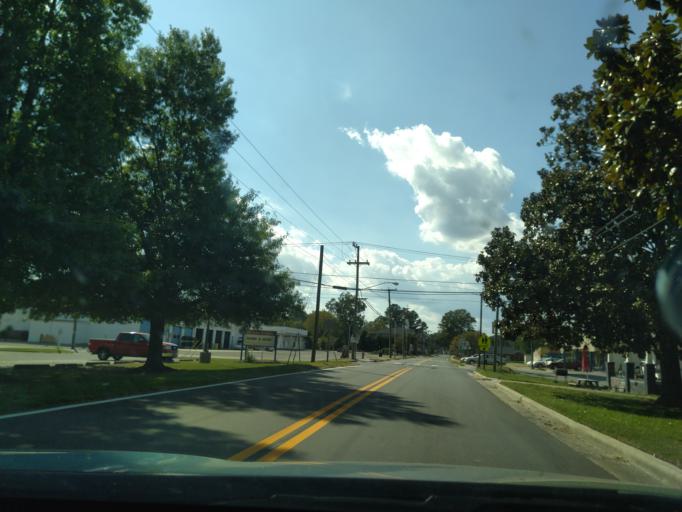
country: US
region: North Carolina
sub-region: Pitt County
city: Bethel
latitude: 35.8068
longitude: -77.3714
